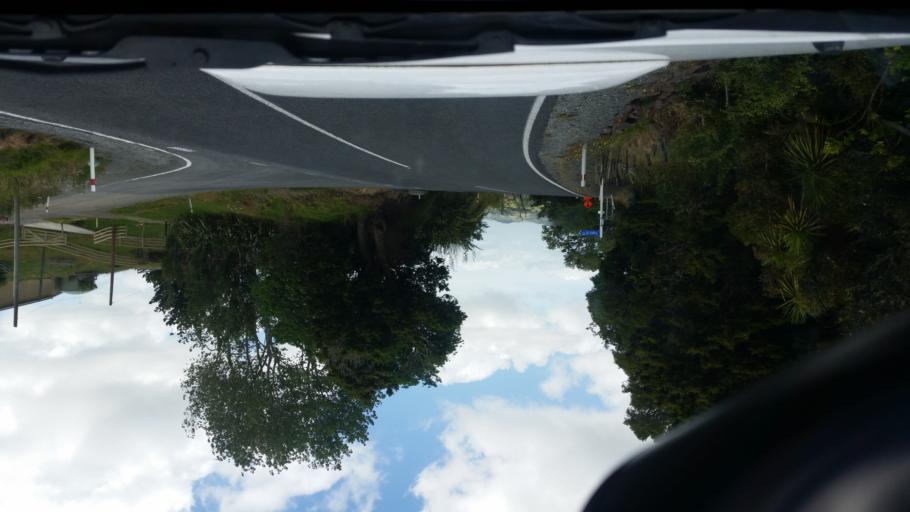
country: NZ
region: Northland
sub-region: Whangarei
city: Ruakaka
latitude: -36.0848
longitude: 174.2400
